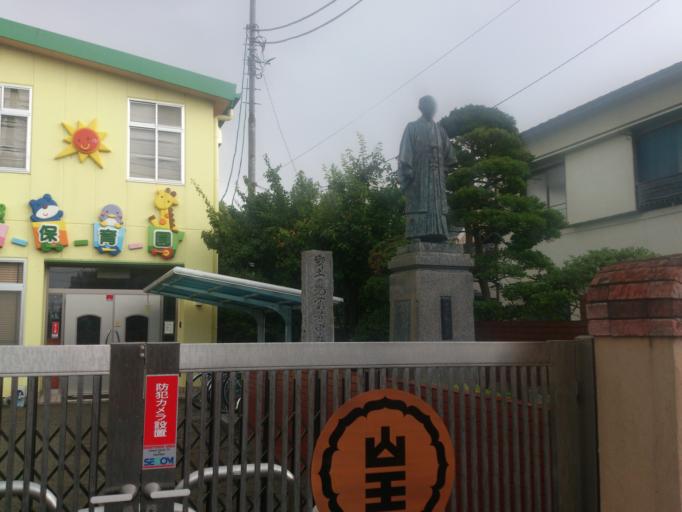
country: JP
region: Chiba
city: Matsudo
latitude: 35.7603
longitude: 139.8568
